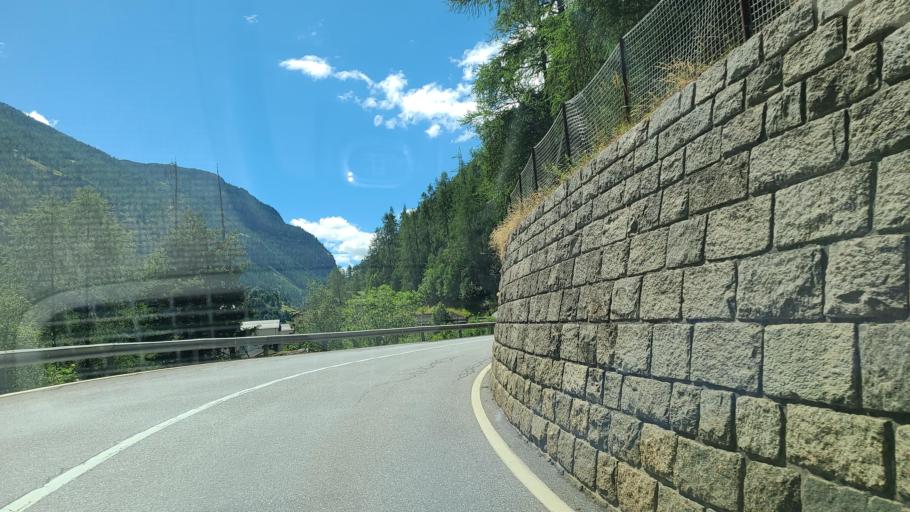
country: CH
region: Valais
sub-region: Visp District
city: Stalden
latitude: 46.2030
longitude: 7.8907
